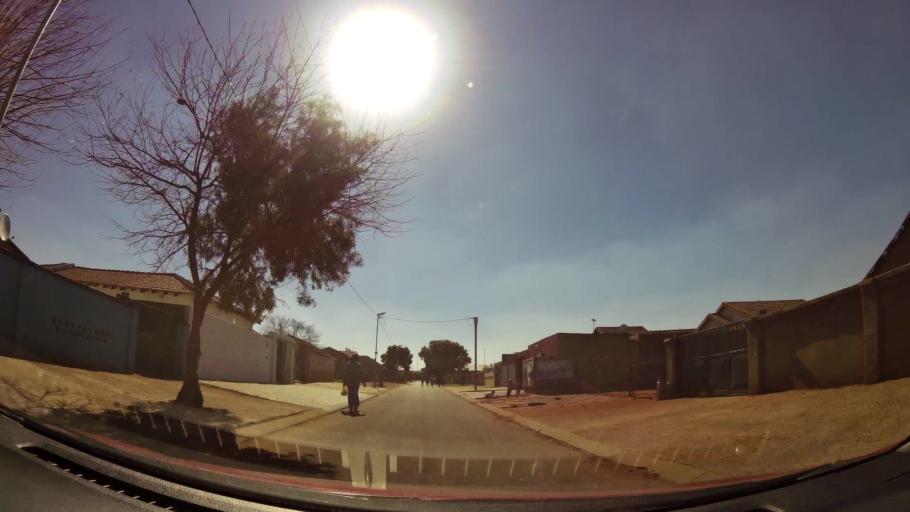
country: ZA
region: Gauteng
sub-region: City of Johannesburg Metropolitan Municipality
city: Soweto
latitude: -26.2501
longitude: 27.8061
